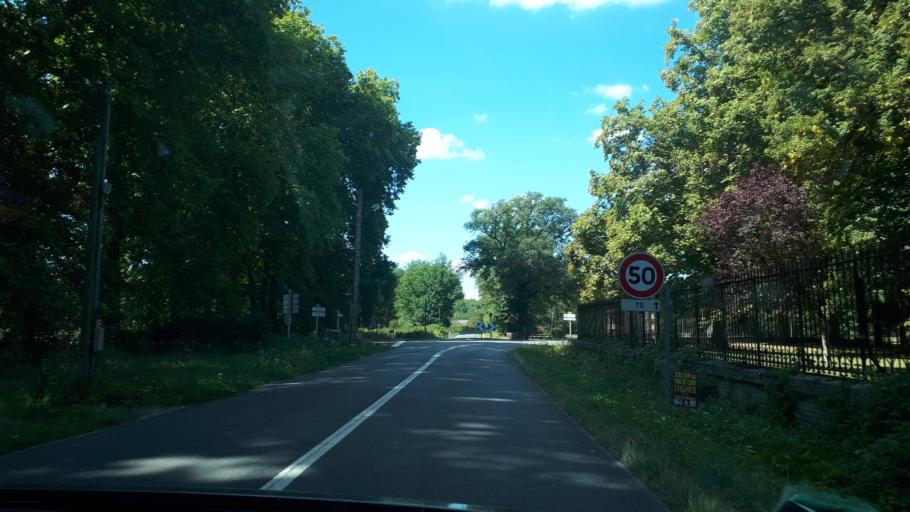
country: FR
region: Centre
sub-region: Departement du Loir-et-Cher
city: Neung-sur-Beuvron
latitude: 47.5317
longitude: 1.8089
